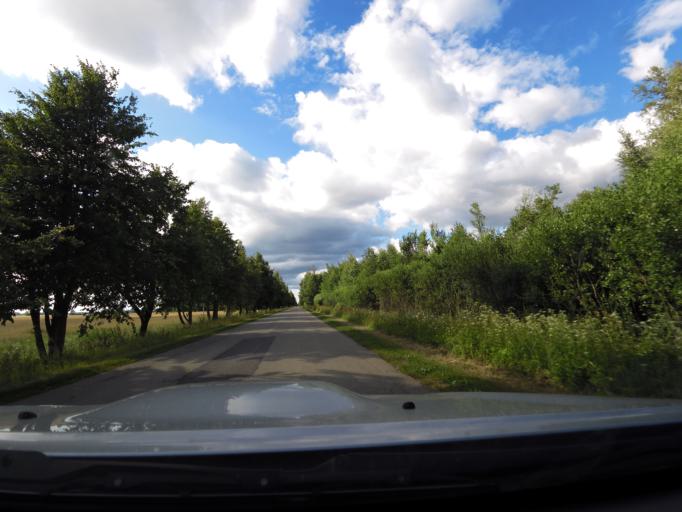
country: LT
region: Panevezys
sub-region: Birzai
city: Birzai
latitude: 56.3556
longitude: 24.7901
